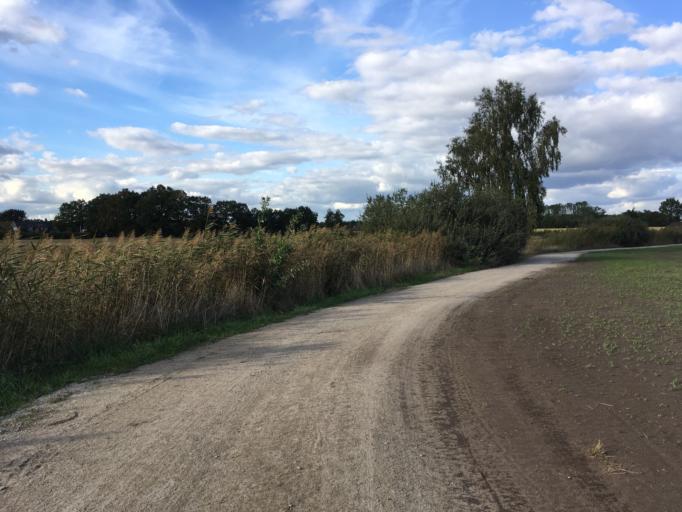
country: DE
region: Lower Saxony
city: Radbruch
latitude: 53.3134
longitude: 10.2946
